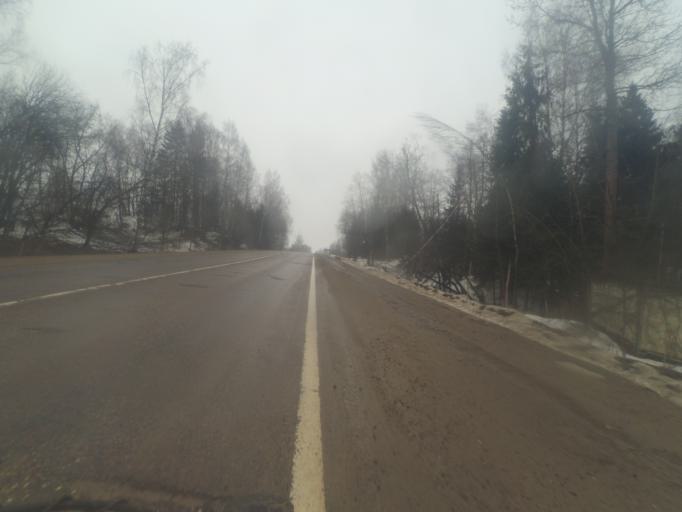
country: RU
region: Moskovskaya
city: Avtopoligon
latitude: 56.2612
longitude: 37.2225
